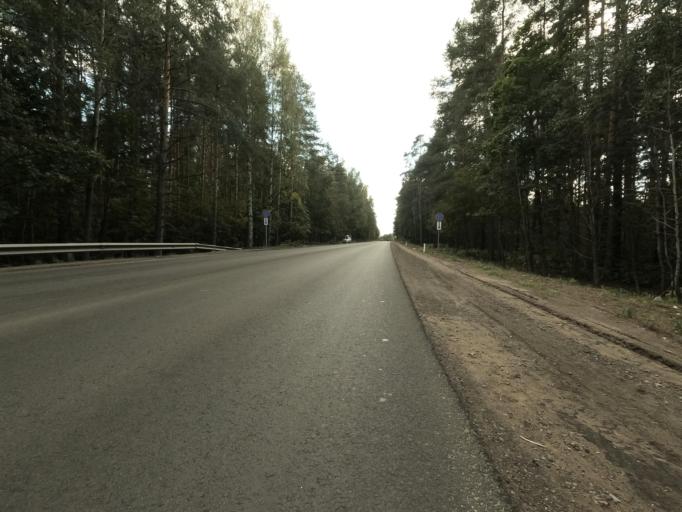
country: RU
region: Leningrad
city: Koltushi
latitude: 59.9576
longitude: 30.6591
